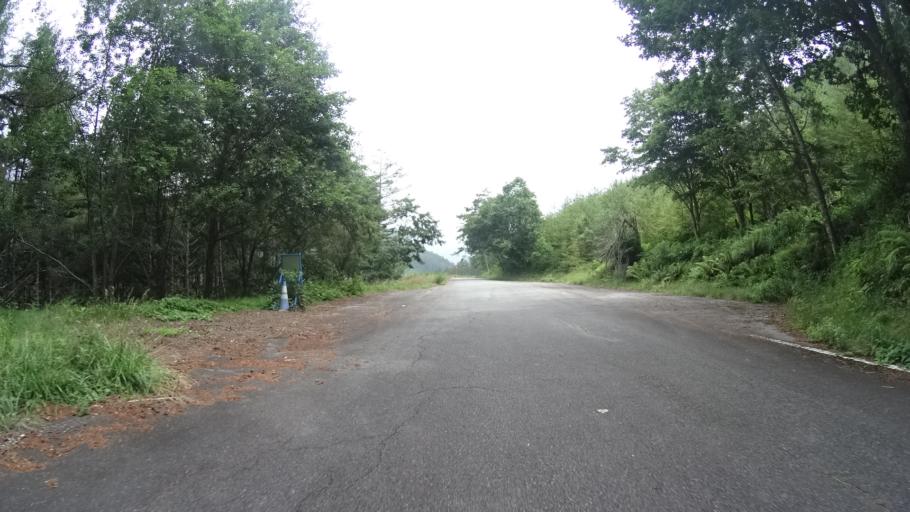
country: JP
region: Yamanashi
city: Kofu-shi
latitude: 35.8309
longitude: 138.5739
